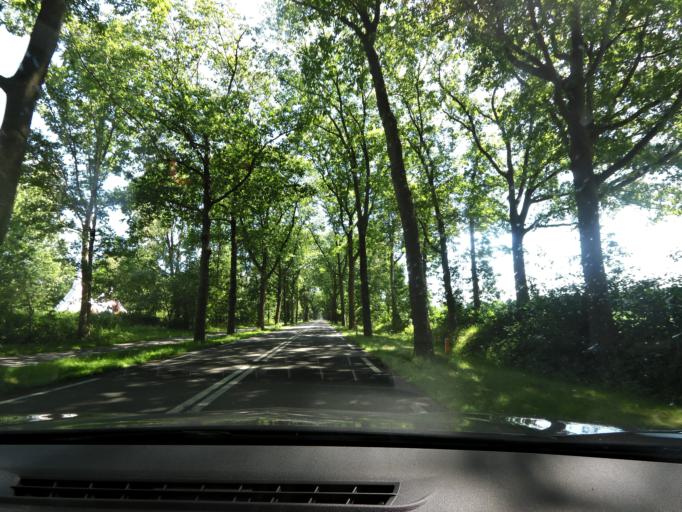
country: NL
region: Gelderland
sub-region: Berkelland
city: Neede
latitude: 52.1644
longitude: 6.5977
